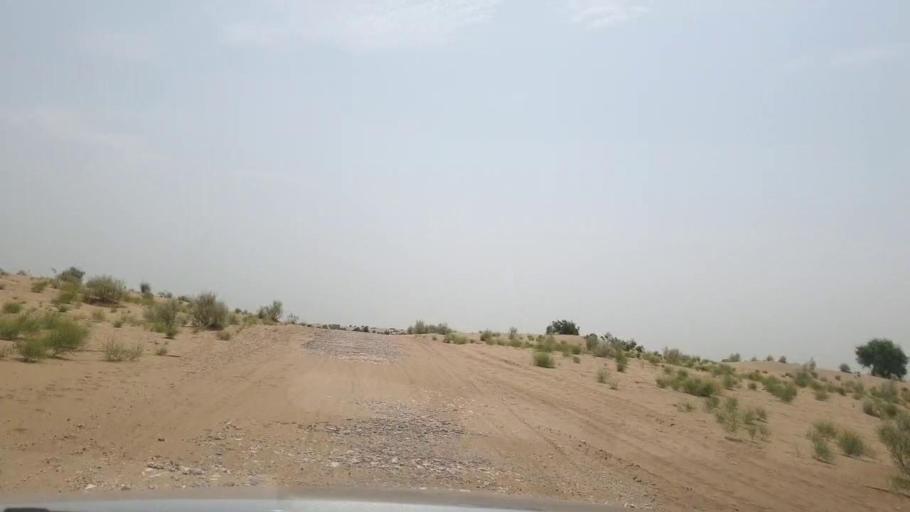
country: PK
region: Sindh
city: Pano Aqil
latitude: 27.5818
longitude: 69.1675
